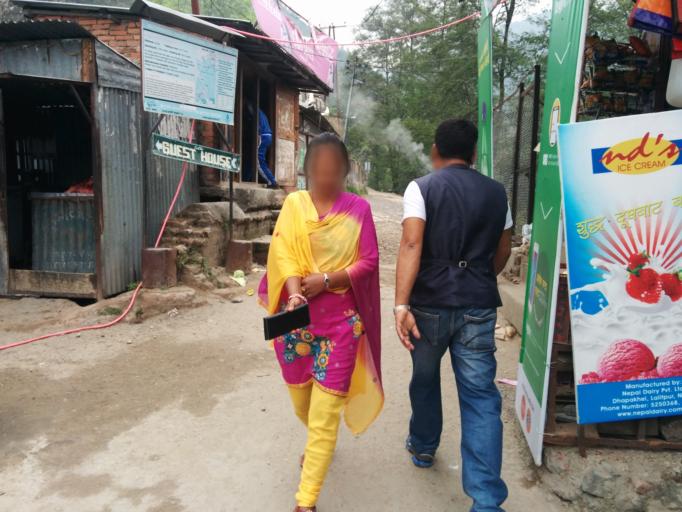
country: NP
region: Central Region
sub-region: Bagmati Zone
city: Bhaktapur
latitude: 27.7594
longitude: 85.4208
